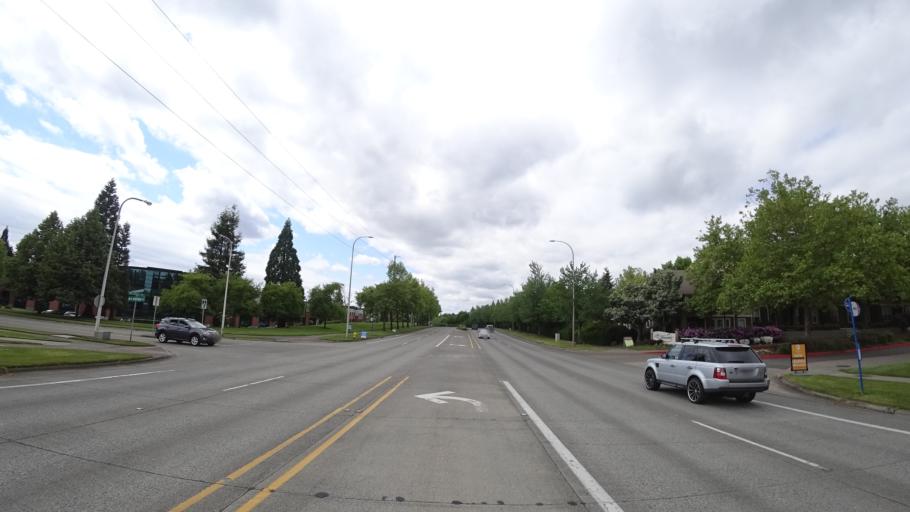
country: US
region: Oregon
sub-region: Washington County
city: Rockcreek
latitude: 45.5369
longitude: -122.8839
